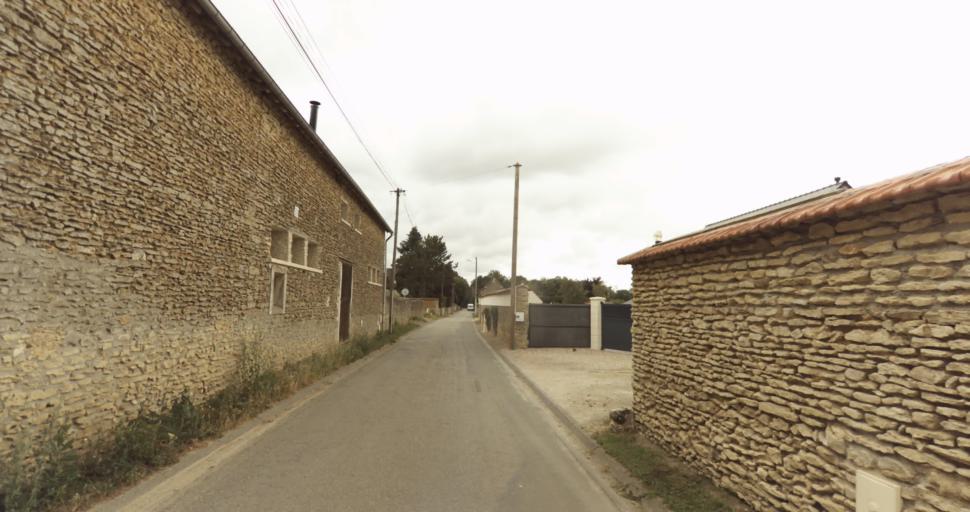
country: FR
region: Haute-Normandie
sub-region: Departement de l'Eure
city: Menilles
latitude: 49.0272
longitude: 1.3070
